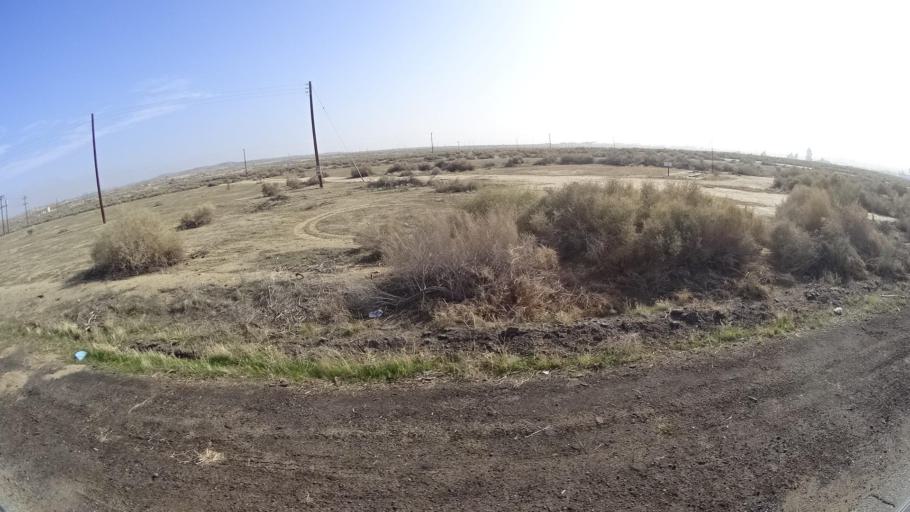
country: US
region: California
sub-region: Kern County
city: Ford City
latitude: 35.1559
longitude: -119.4269
